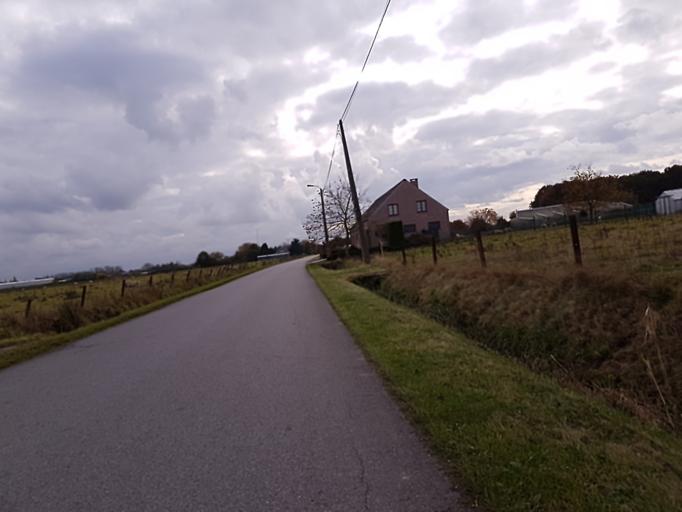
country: BE
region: Flanders
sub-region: Provincie Antwerpen
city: Lint
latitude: 51.1272
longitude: 4.5318
